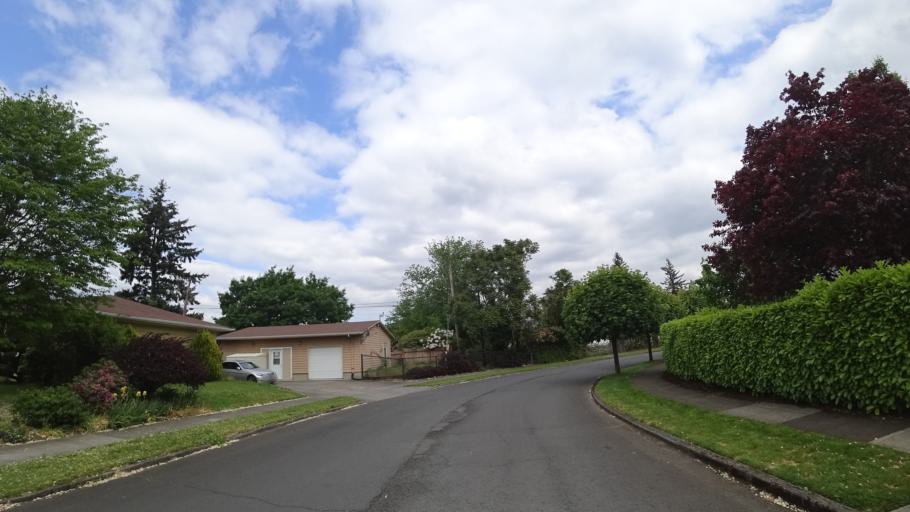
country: US
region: Oregon
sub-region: Multnomah County
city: Fairview
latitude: 45.5158
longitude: -122.4917
